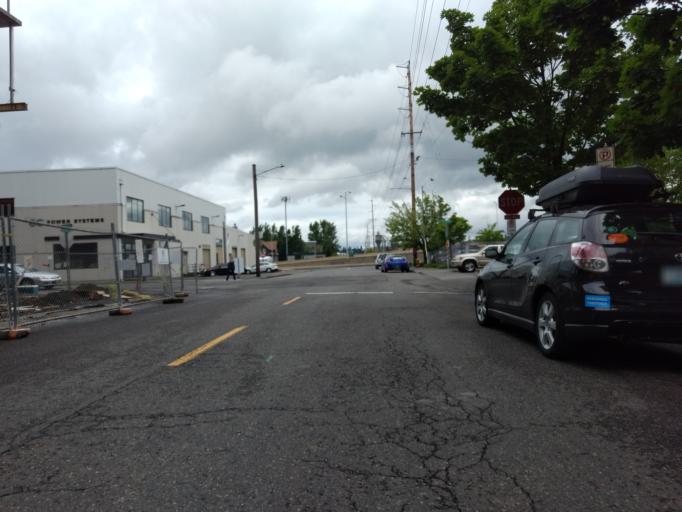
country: US
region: Oregon
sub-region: Multnomah County
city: Portland
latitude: 45.5353
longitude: -122.6948
